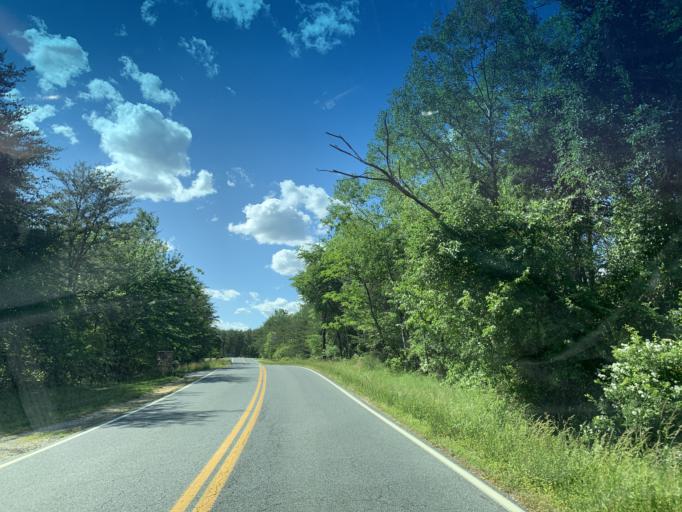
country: US
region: Maryland
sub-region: Cecil County
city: North East
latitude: 39.5568
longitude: -75.9247
